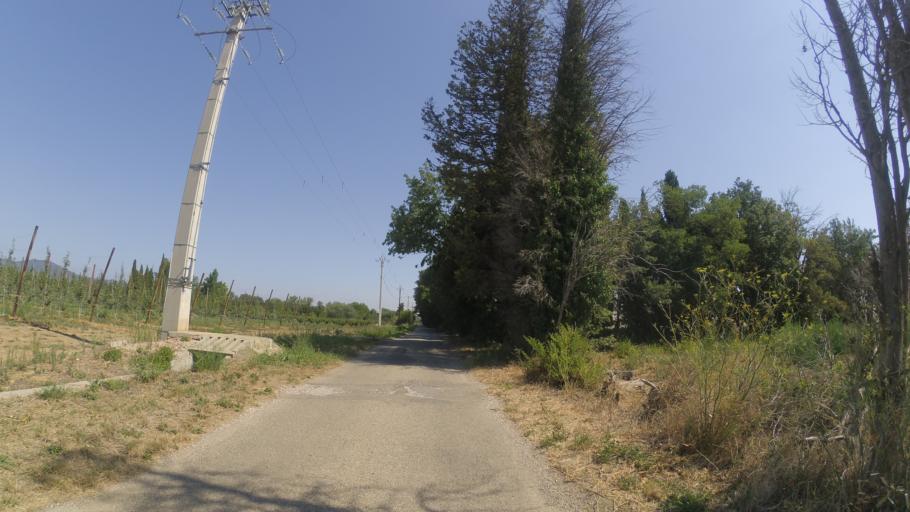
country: FR
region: Languedoc-Roussillon
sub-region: Departement des Pyrenees-Orientales
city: Corneilla-la-Riviere
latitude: 42.6715
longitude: 2.7321
